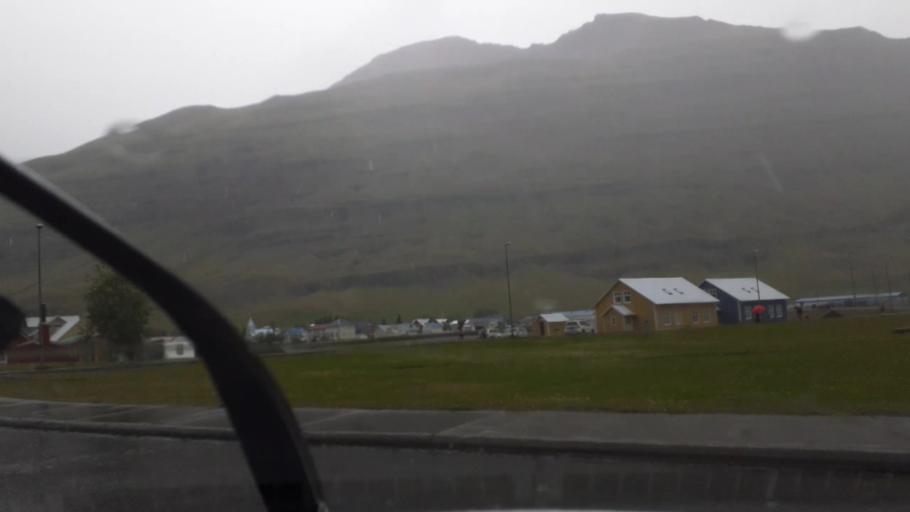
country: IS
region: East
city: Eskifjoerdur
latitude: 65.2616
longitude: -13.9998
